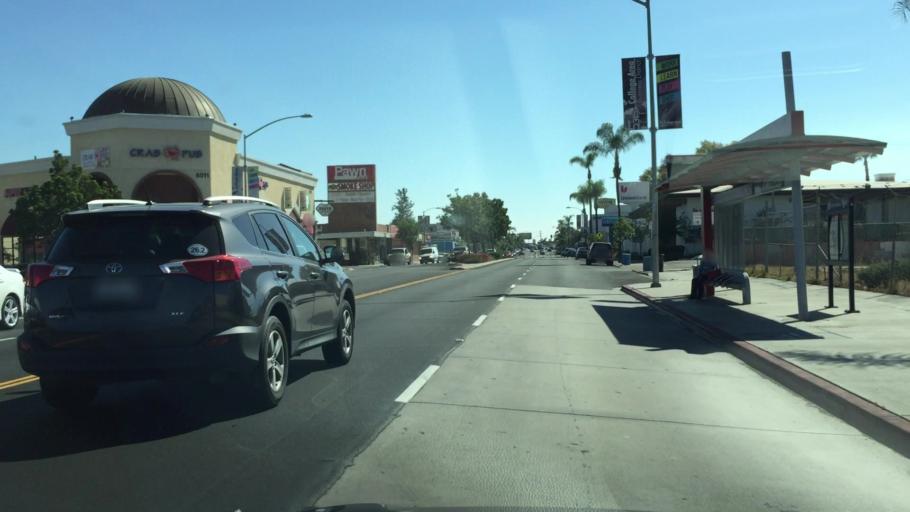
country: US
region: California
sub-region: San Diego County
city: Lemon Grove
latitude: 32.7612
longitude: -117.0675
